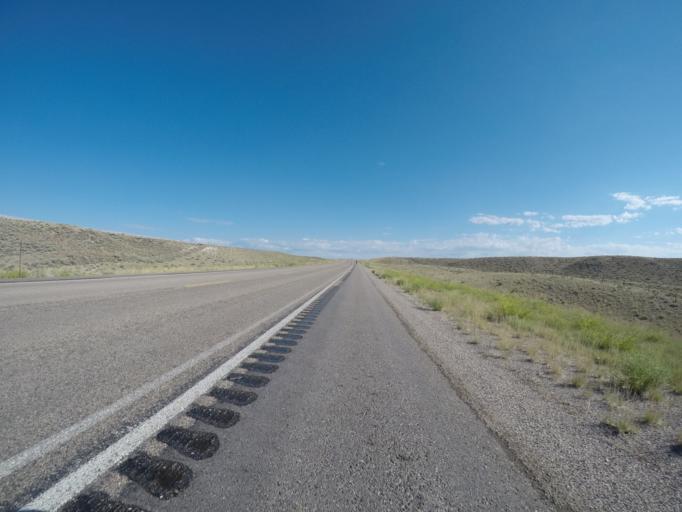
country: US
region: Wyoming
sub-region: Lincoln County
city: Kemmerer
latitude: 42.0464
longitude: -110.1606
